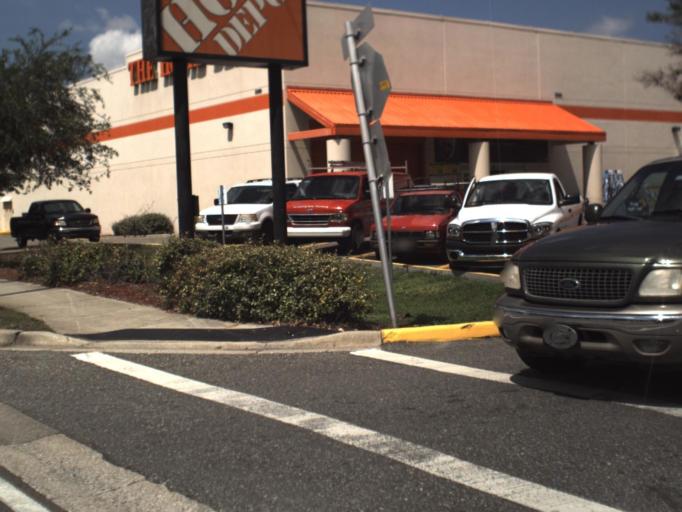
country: US
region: Florida
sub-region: Manatee County
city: South Bradenton
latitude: 27.4625
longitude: -82.5841
